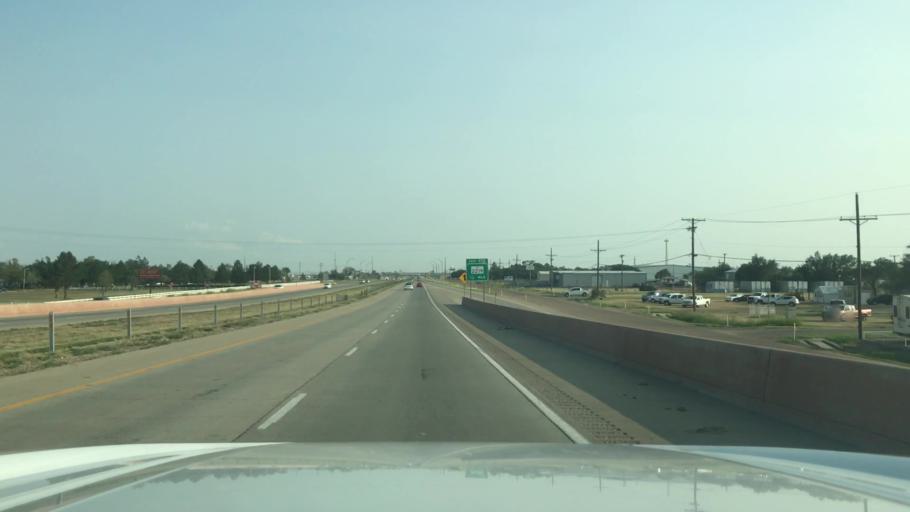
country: US
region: Texas
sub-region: Randall County
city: Canyon
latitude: 35.0697
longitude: -101.9194
